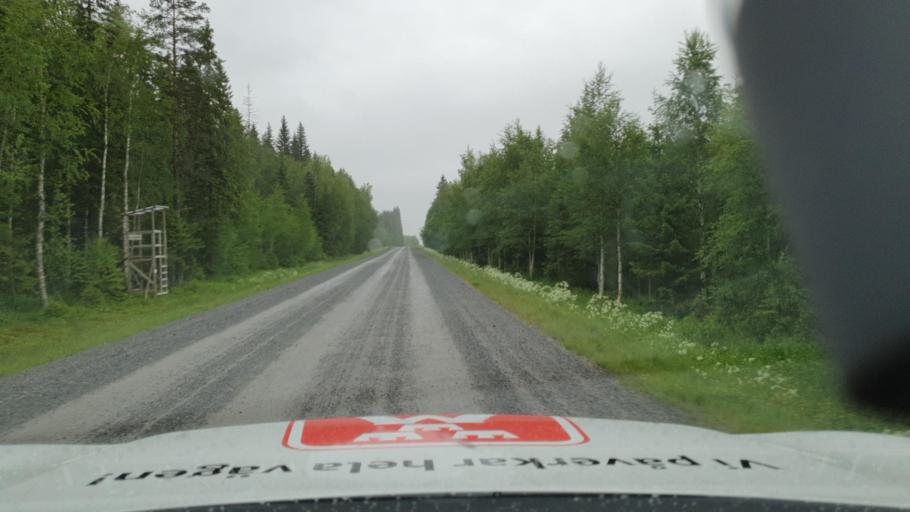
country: SE
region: Vaesterbotten
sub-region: Nordmalings Kommun
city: Nordmaling
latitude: 63.8267
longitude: 19.4903
